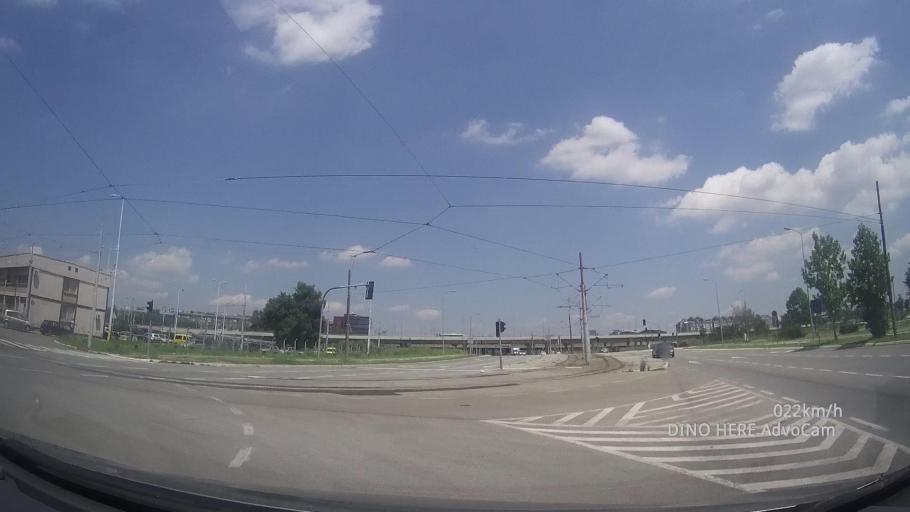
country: RS
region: Central Serbia
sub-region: Belgrade
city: Novi Beograd
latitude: 44.8066
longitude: 20.4110
